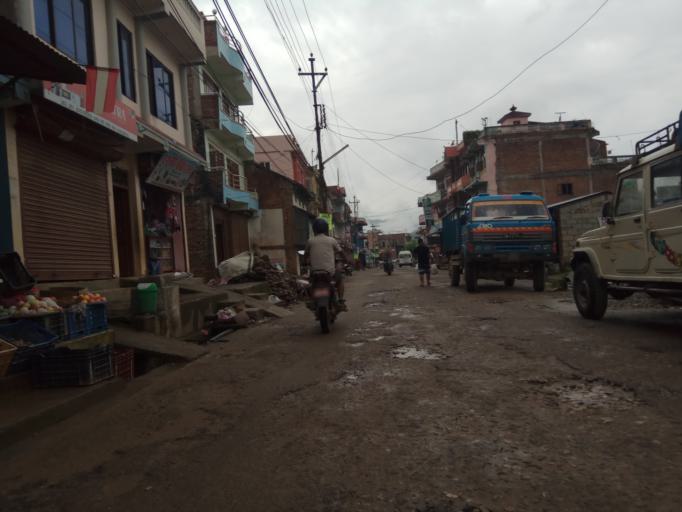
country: NP
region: Central Region
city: Kirtipur
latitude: 27.9086
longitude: 84.9011
